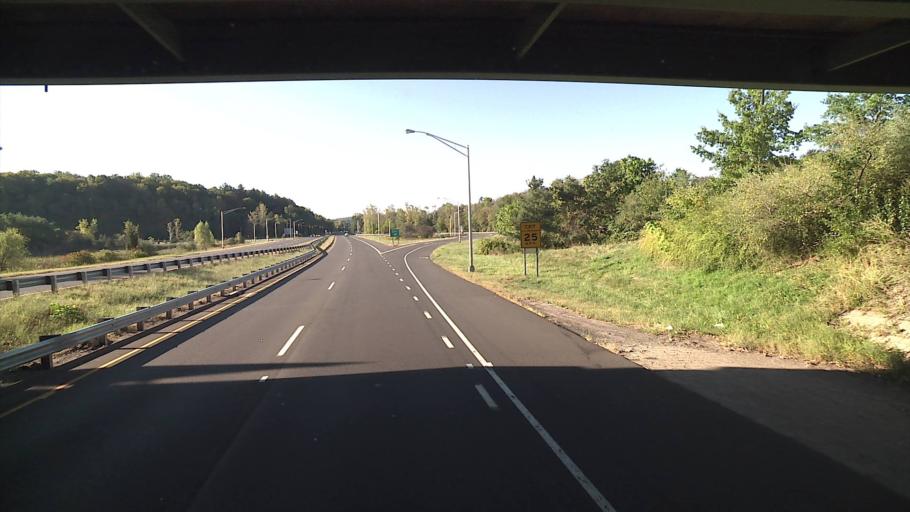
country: US
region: Connecticut
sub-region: Hartford County
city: Kensington
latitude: 41.6249
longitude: -72.7412
